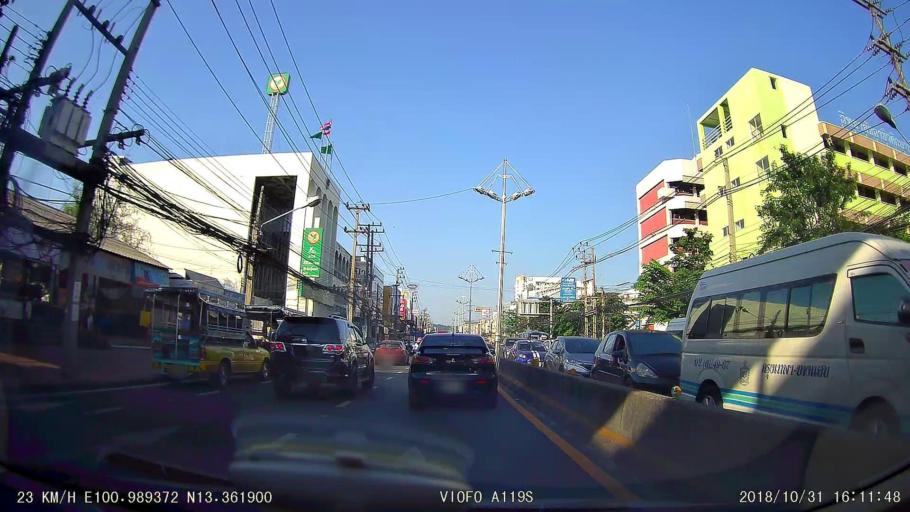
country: TH
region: Chon Buri
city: Chon Buri
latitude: 13.3619
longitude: 100.9894
